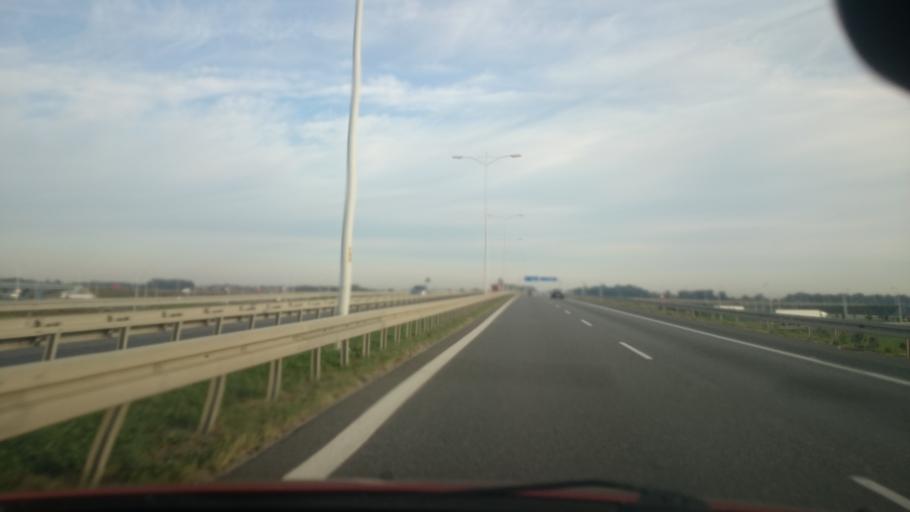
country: PL
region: Lower Silesian Voivodeship
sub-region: Powiat wroclawski
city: Tyniec Maly
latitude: 51.0419
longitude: 16.9356
